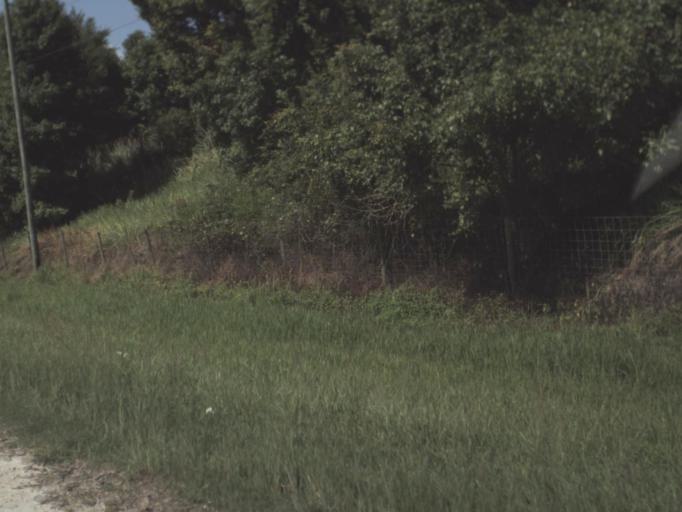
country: US
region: Florida
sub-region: Hernando County
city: North Brooksville
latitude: 28.5742
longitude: -82.4210
